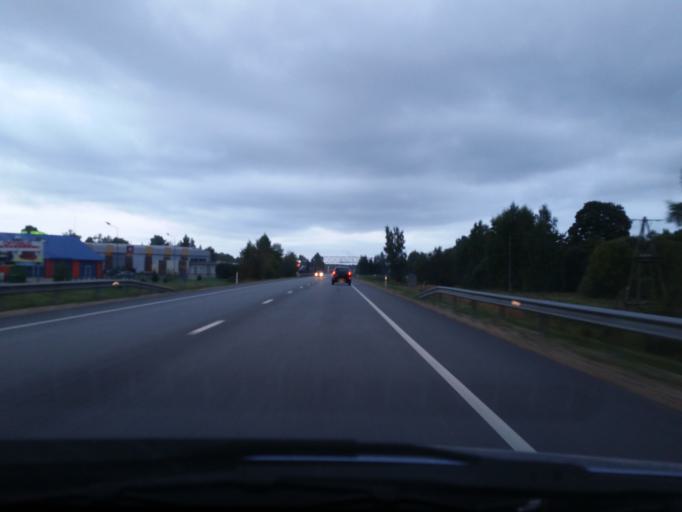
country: LV
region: Adazi
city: Adazi
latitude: 57.0822
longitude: 24.3157
